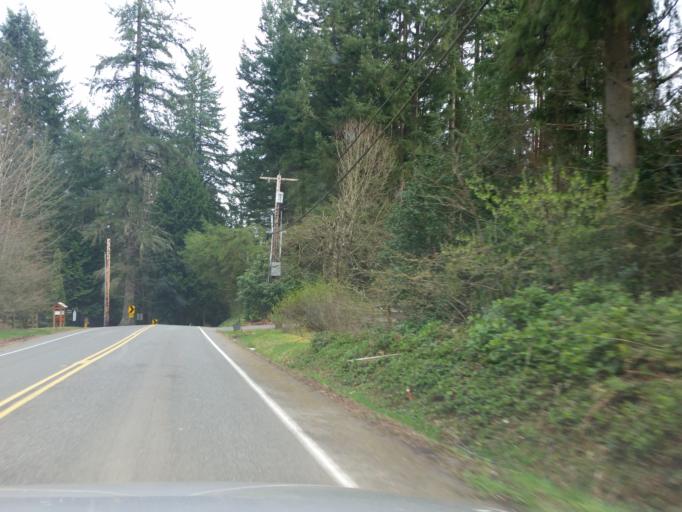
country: US
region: Washington
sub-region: King County
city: Cottage Lake
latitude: 47.7519
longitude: -122.1123
